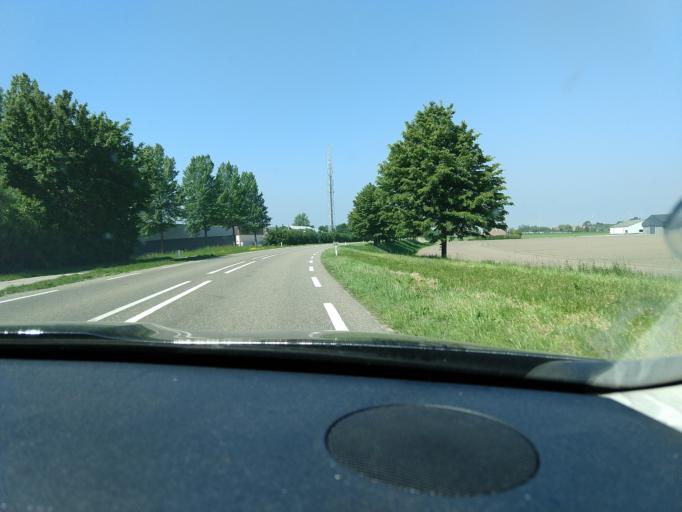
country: NL
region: Zeeland
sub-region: Gemeente Reimerswaal
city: Yerseke
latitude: 51.5486
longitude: 4.0949
